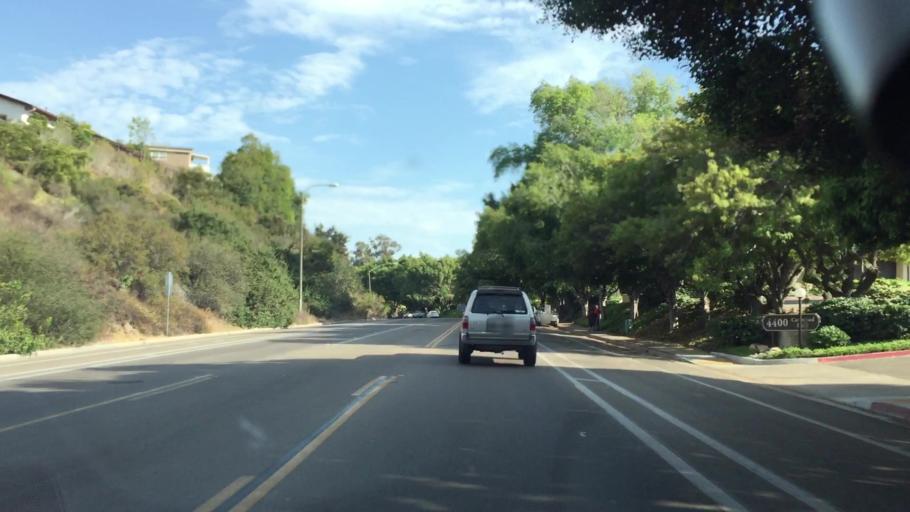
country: US
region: California
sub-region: San Diego County
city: Lemon Grove
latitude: 32.7645
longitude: -117.0835
